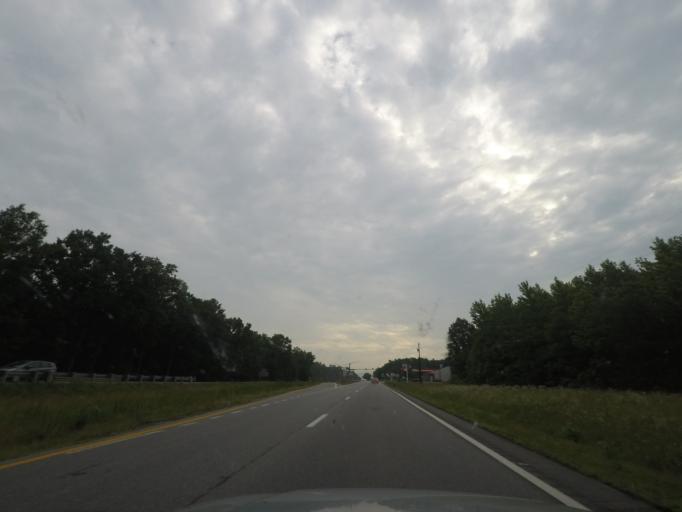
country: US
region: Virginia
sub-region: Mecklenburg County
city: Chase City
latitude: 36.9024
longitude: -78.5365
